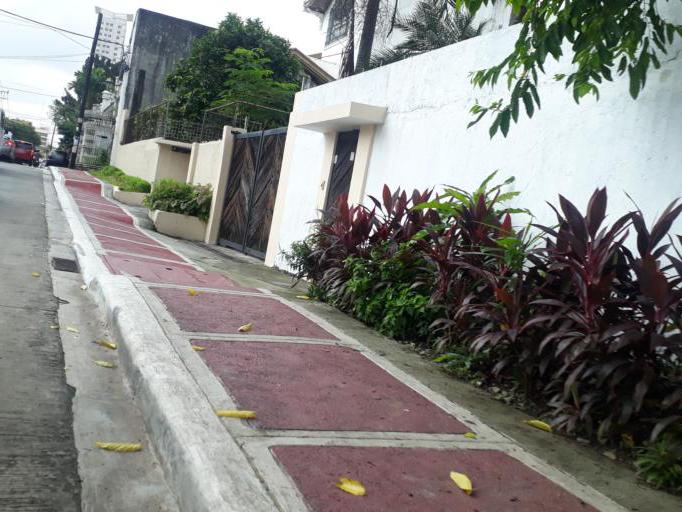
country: PH
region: Metro Manila
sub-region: San Juan
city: San Juan
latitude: 14.6151
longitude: 121.0280
